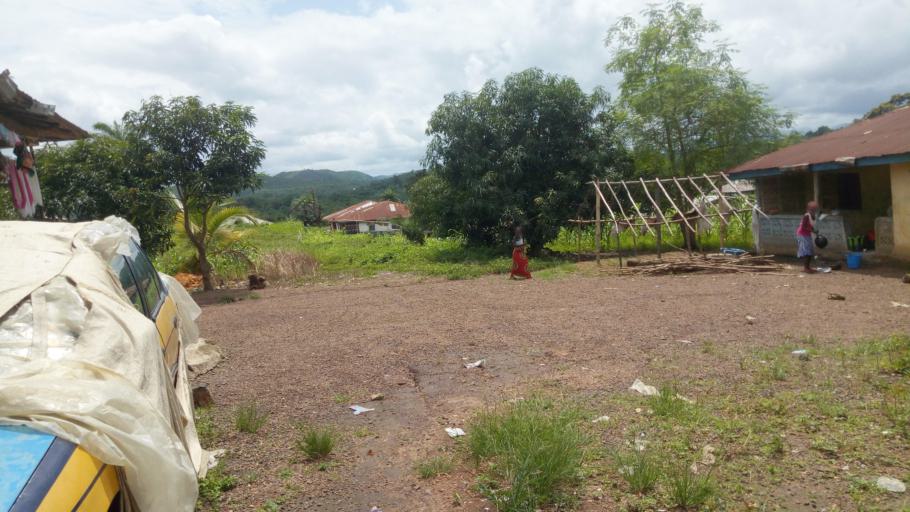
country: SL
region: Northern Province
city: Magburaka
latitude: 8.7191
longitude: -11.9619
